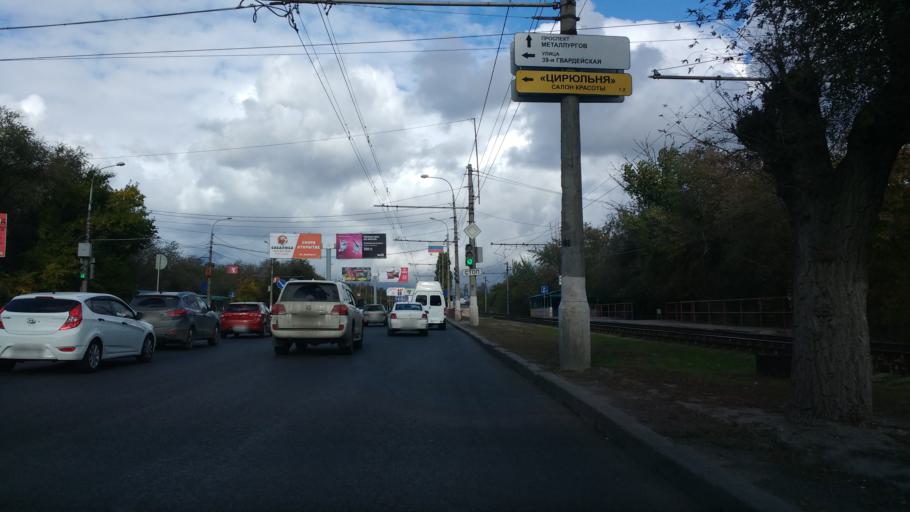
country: RU
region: Volgograd
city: Krasnoslobodsk
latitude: 48.7563
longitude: 44.5539
